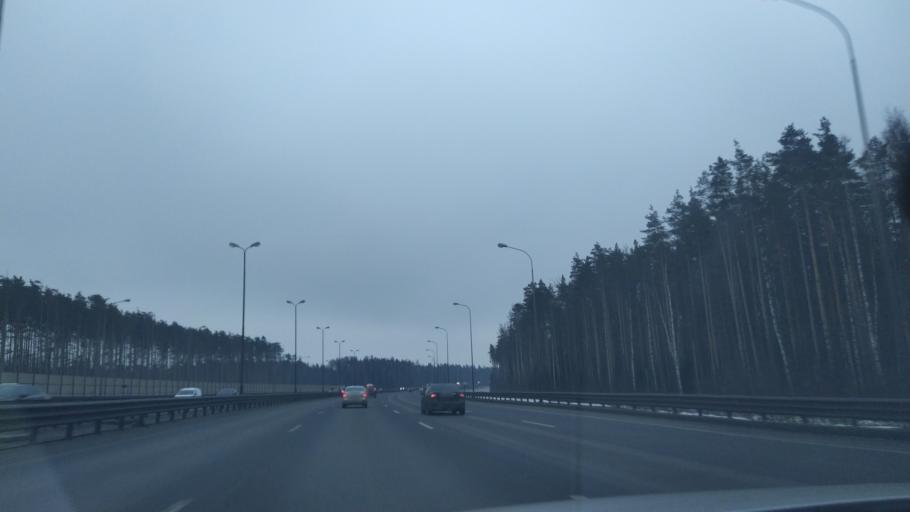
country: RU
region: St.-Petersburg
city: Krasnogvargeisky
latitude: 59.9715
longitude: 30.5477
